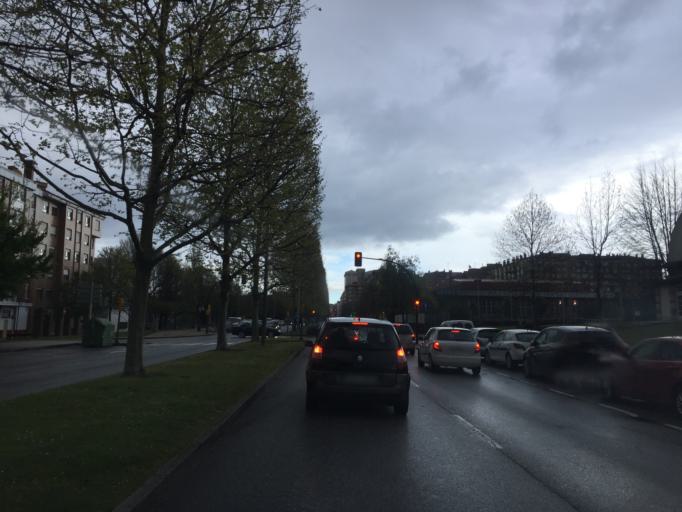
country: ES
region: Asturias
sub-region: Province of Asturias
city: Gijon
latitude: 43.5258
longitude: -5.6629
